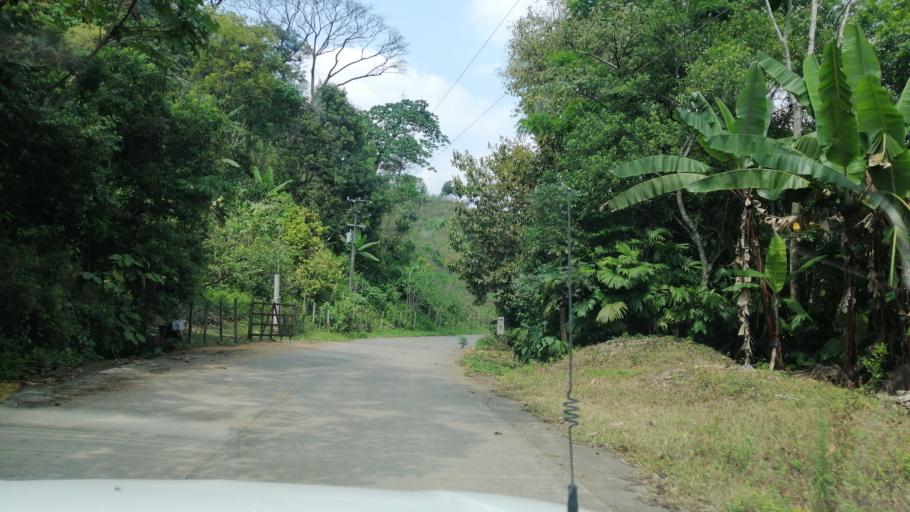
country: MX
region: Chiapas
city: Ostuacan
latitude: 17.3919
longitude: -93.3305
